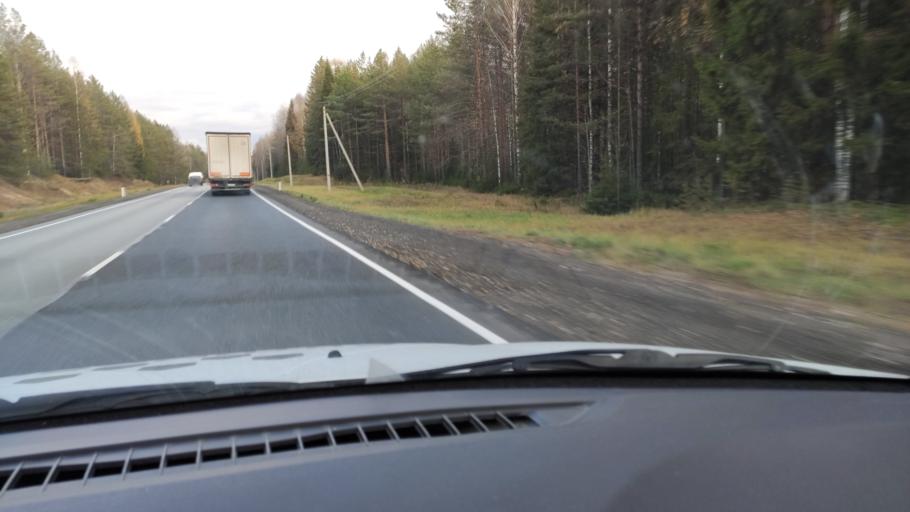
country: RU
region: Kirov
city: Belaya Kholunitsa
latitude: 58.9143
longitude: 51.1582
